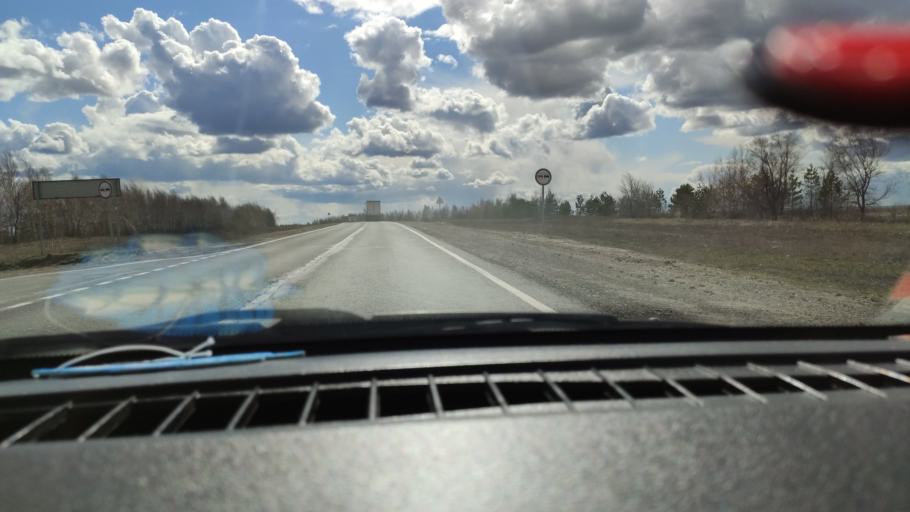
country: RU
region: Saratov
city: Dukhovnitskoye
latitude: 52.8346
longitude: 48.2409
